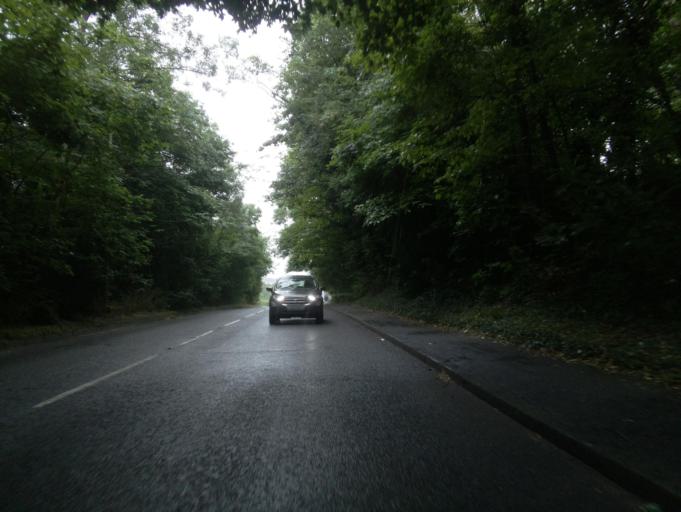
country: GB
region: England
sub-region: Surrey
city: Salfords
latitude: 51.2219
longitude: -0.1724
